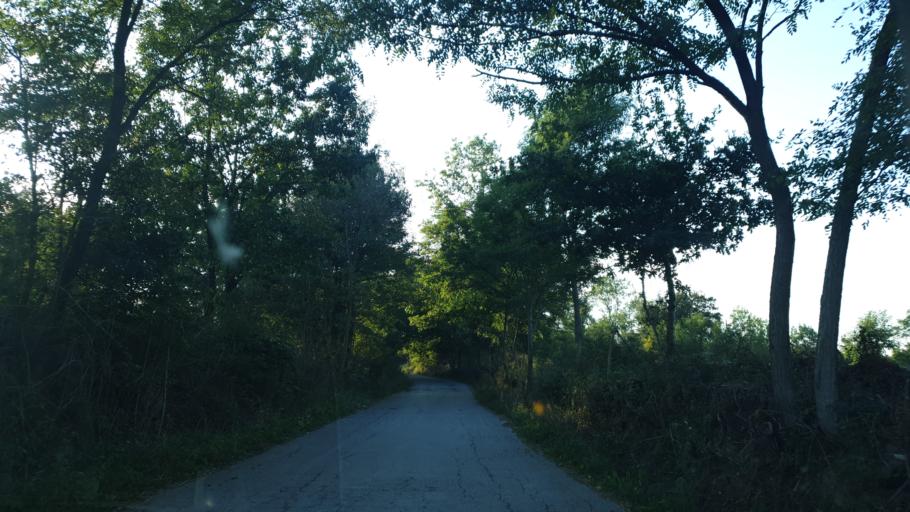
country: RS
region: Central Serbia
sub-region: Zlatiborski Okrug
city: Kosjeric
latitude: 43.9753
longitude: 20.0218
